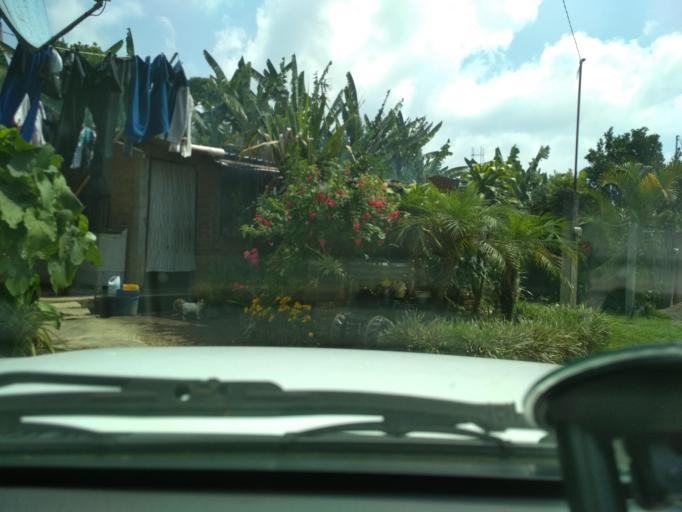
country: MX
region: Veracruz
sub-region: Fortin
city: Santa Lucia Potrerillo
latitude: 18.9692
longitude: -97.0266
